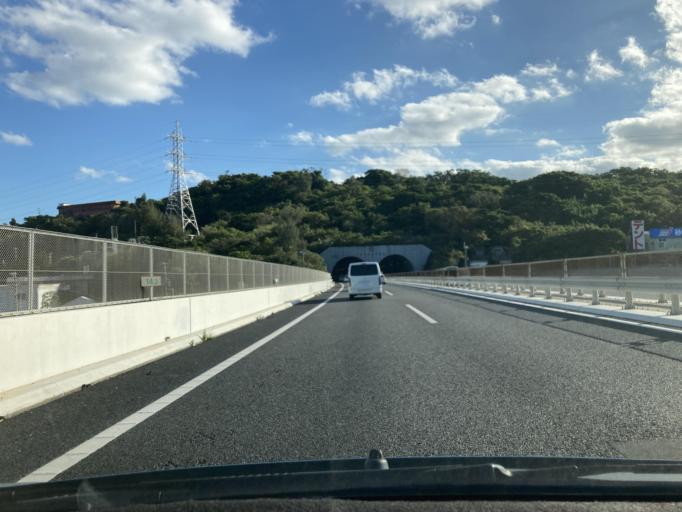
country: JP
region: Okinawa
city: Chatan
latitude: 26.3100
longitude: 127.7882
